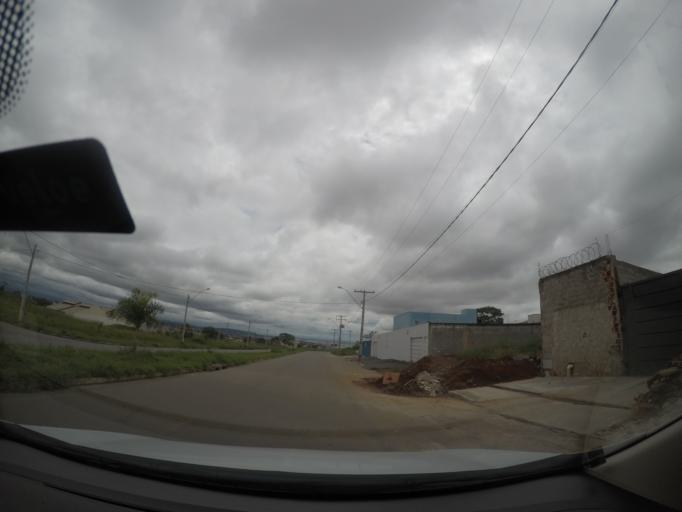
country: BR
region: Goias
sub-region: Goiania
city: Goiania
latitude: -16.7497
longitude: -49.3380
